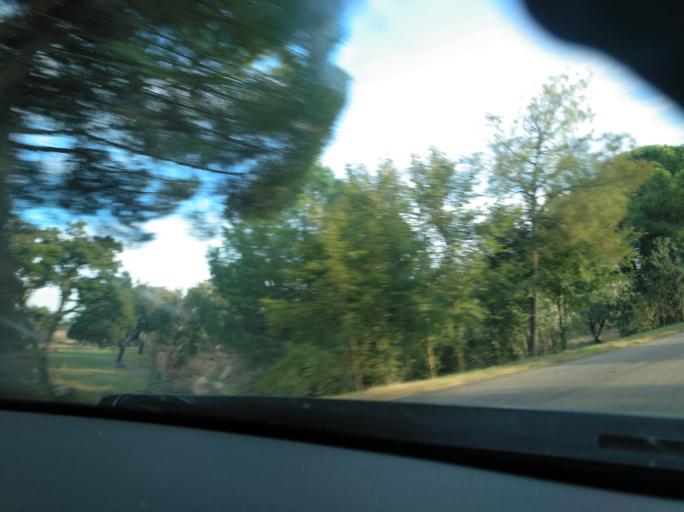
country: PT
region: Portalegre
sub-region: Avis
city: Avis
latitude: 38.8587
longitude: -7.8263
